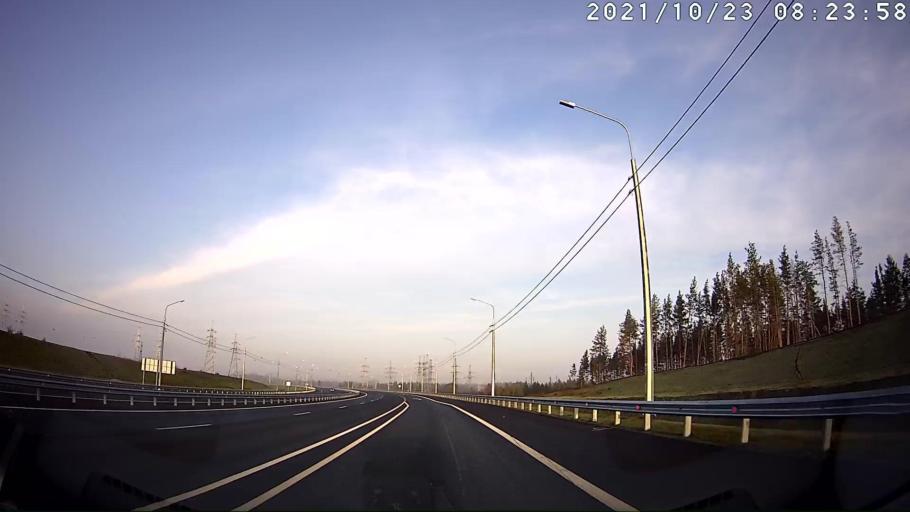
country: RU
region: Saratov
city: Sennoy
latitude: 52.1435
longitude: 46.9145
